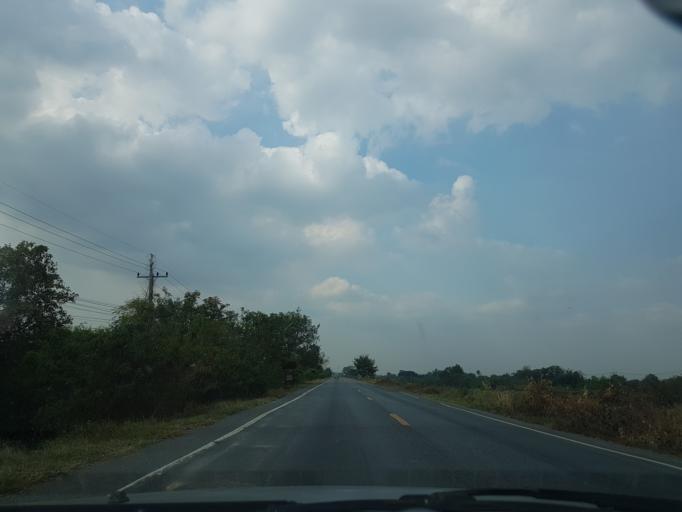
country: TH
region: Phra Nakhon Si Ayutthaya
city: Phachi
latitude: 14.4731
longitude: 100.7464
